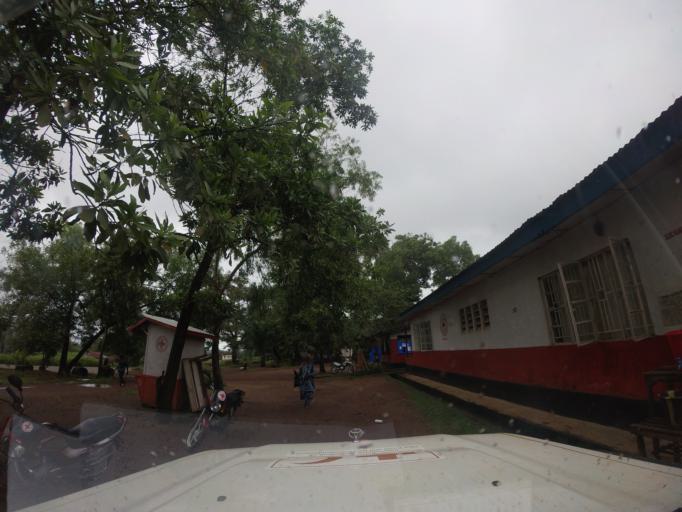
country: SL
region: Northern Province
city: Kambia
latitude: 9.1142
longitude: -12.9237
